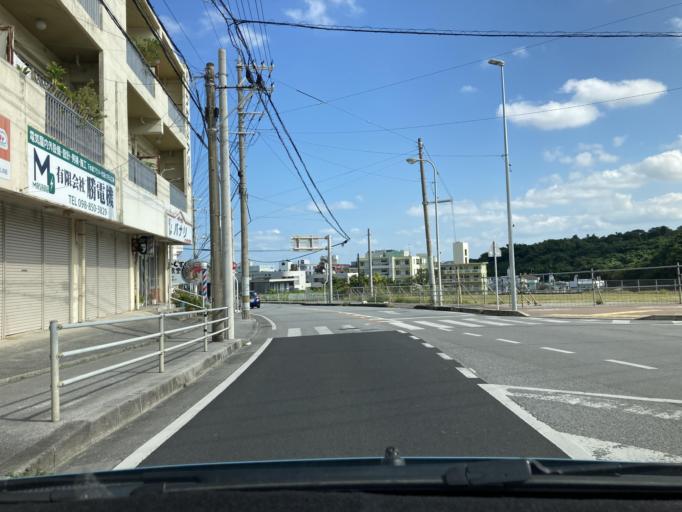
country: JP
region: Okinawa
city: Tomigusuku
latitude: 26.1879
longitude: 127.6804
